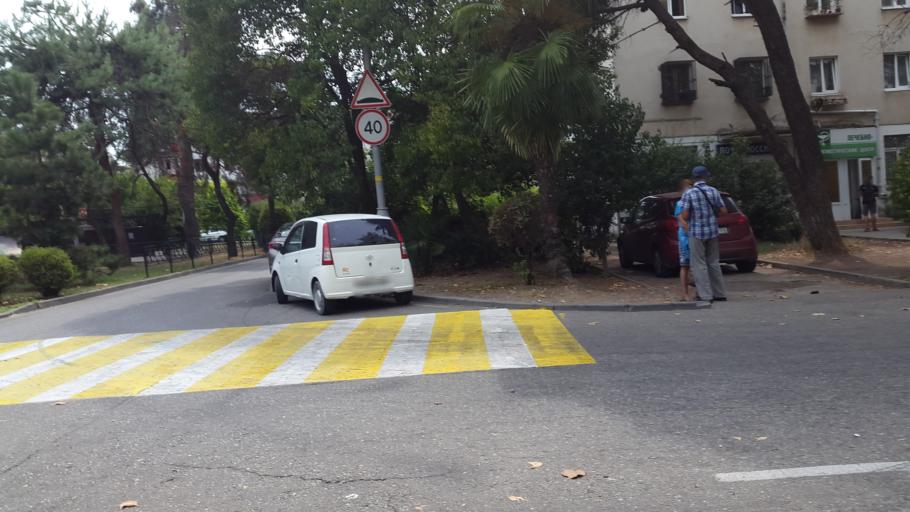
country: RU
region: Krasnodarskiy
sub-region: Sochi City
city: Sochi
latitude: 43.6021
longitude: 39.7243
